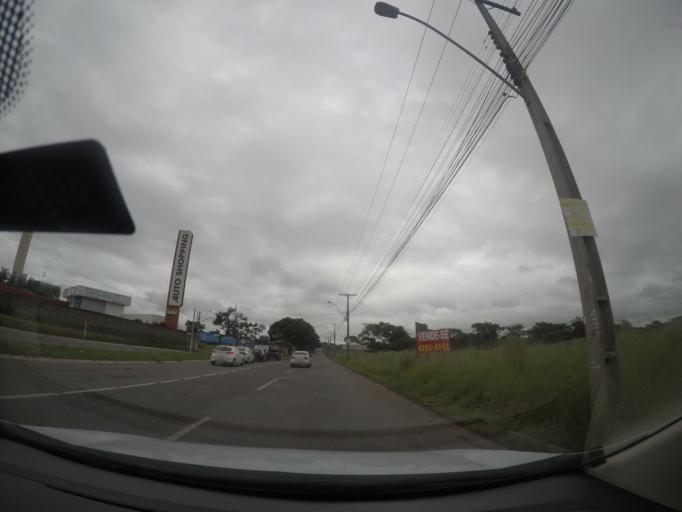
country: BR
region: Goias
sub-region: Goiania
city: Goiania
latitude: -16.7479
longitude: -49.3063
